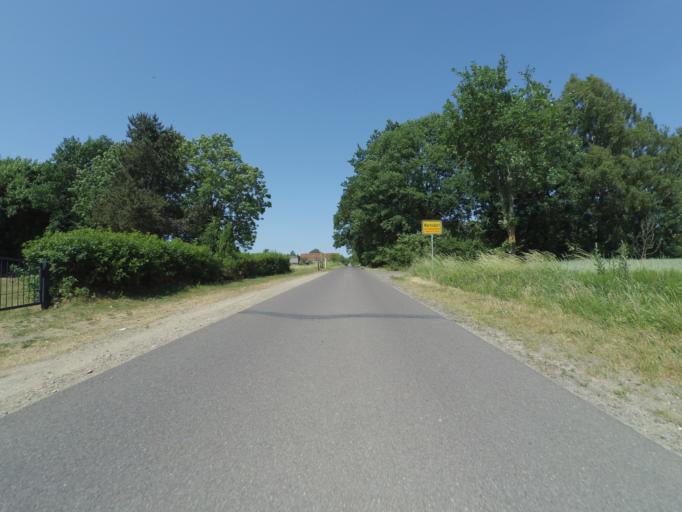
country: DE
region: Brandenburg
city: Gerdshagen
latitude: 53.2586
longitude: 12.2828
